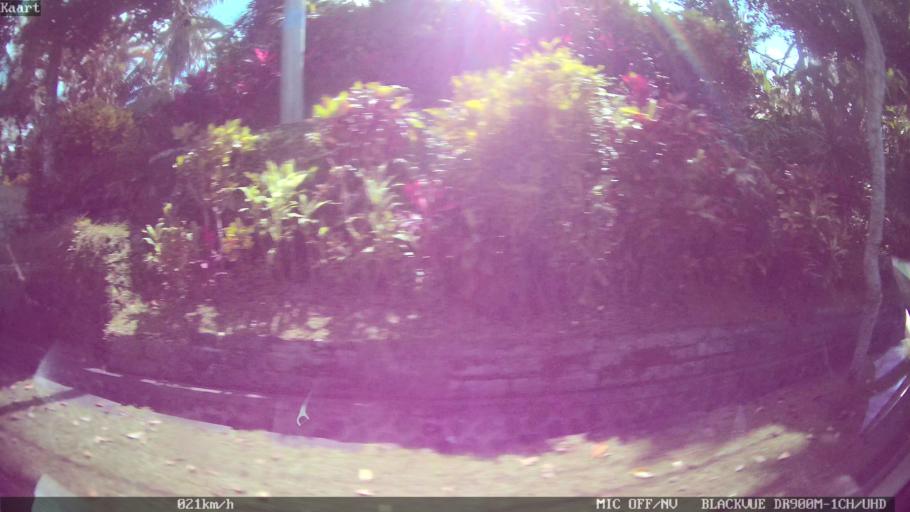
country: ID
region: Bali
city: Banjar Kelodan
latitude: -8.5165
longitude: 115.3338
